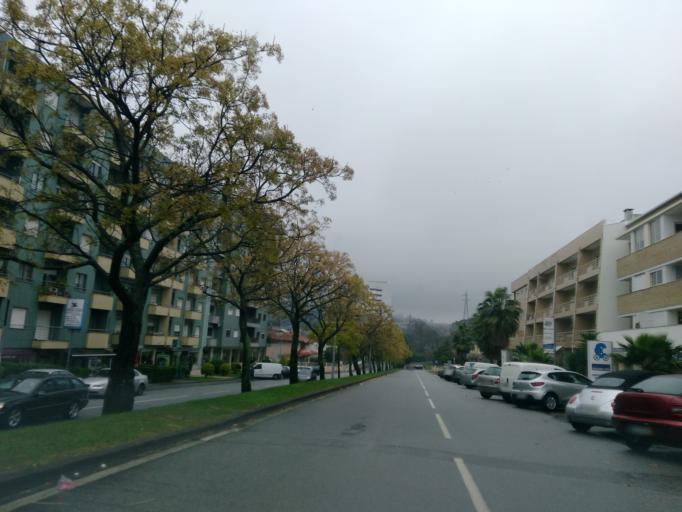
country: PT
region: Braga
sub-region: Braga
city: Braga
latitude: 41.5534
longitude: -8.3951
